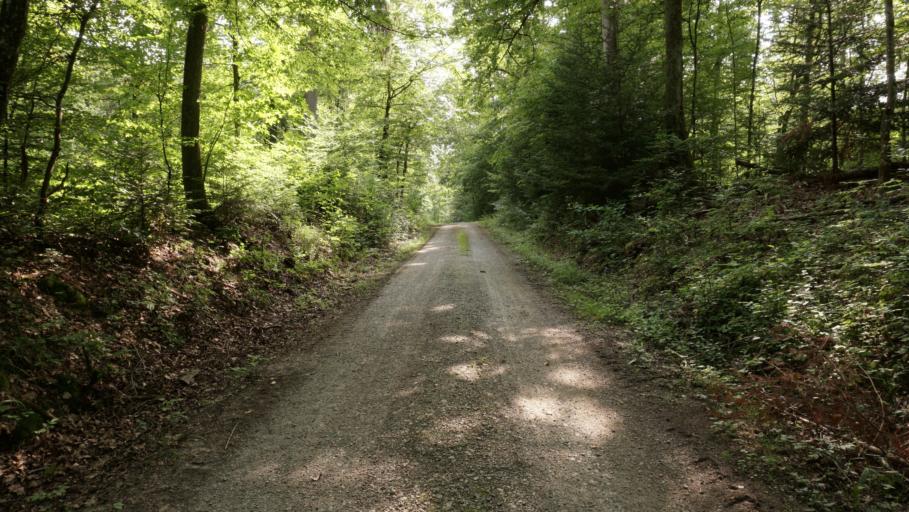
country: DE
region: Baden-Wuerttemberg
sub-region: Regierungsbezirk Stuttgart
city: Gundelsheim
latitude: 49.3120
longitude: 9.1928
